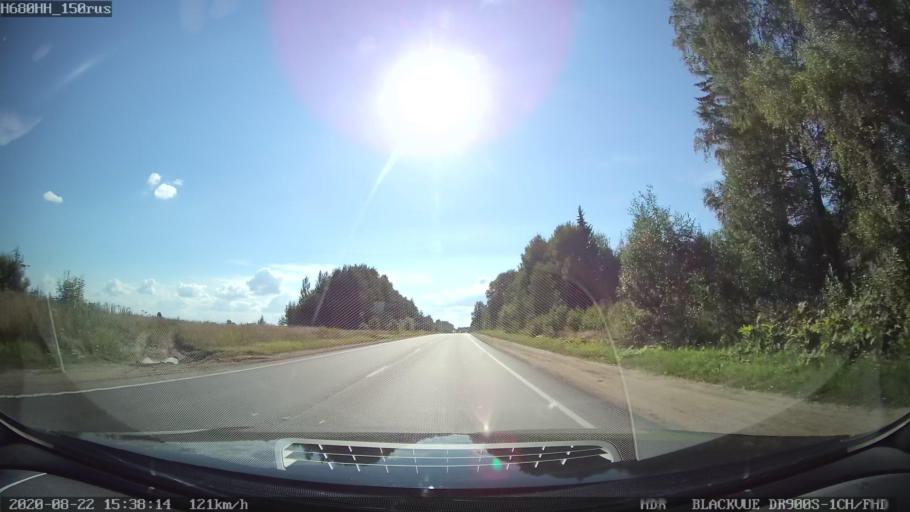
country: RU
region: Tverskaya
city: Bezhetsk
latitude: 57.7644
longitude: 36.6546
